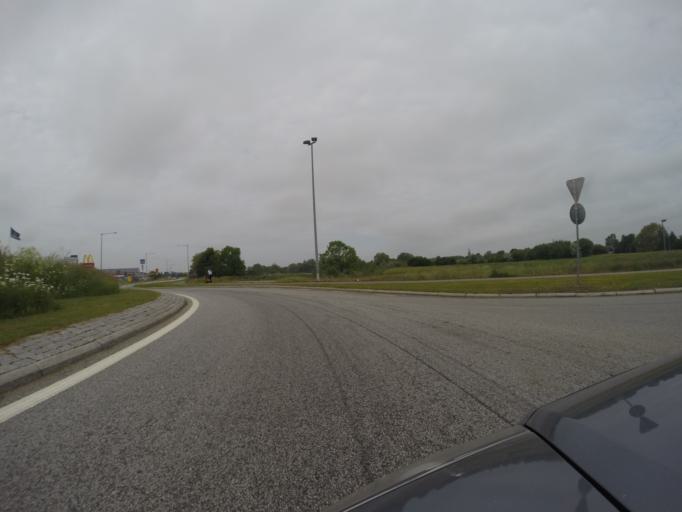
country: SE
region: Skane
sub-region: Lomma Kommun
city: Lomma
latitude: 55.6857
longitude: 13.0917
